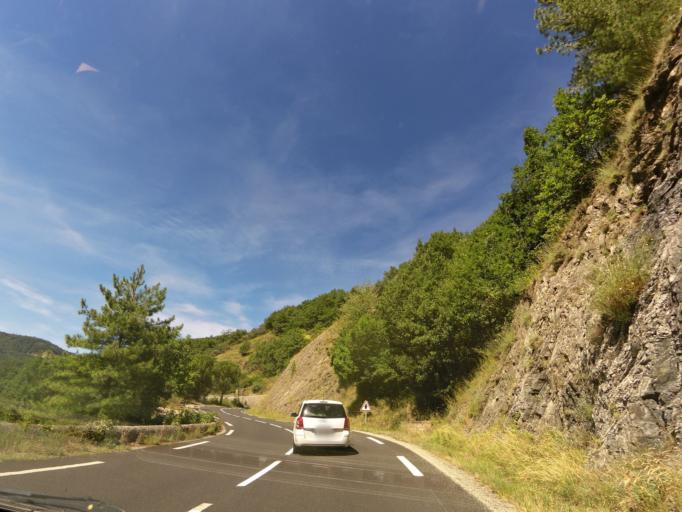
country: FR
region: Languedoc-Roussillon
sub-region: Departement du Gard
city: Le Vigan
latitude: 43.9789
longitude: 3.4751
